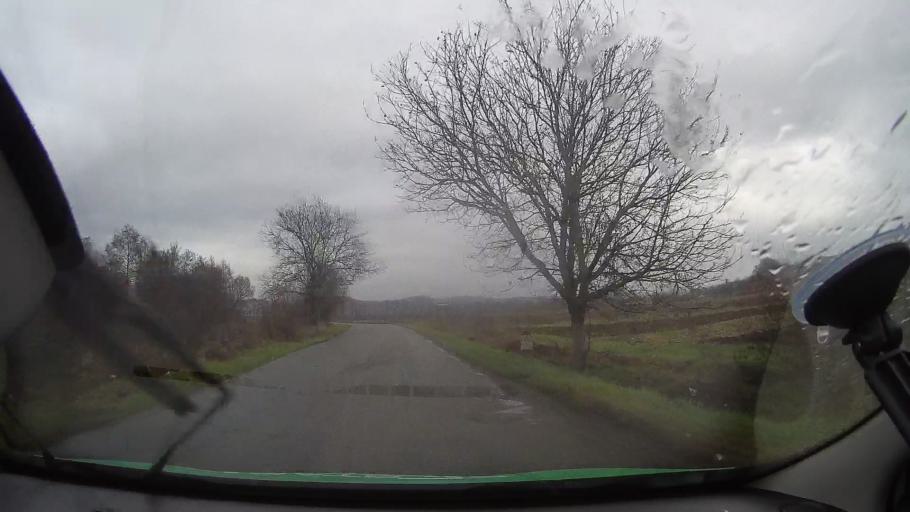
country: RO
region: Hunedoara
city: Vata de Jos
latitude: 46.1834
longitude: 22.6049
